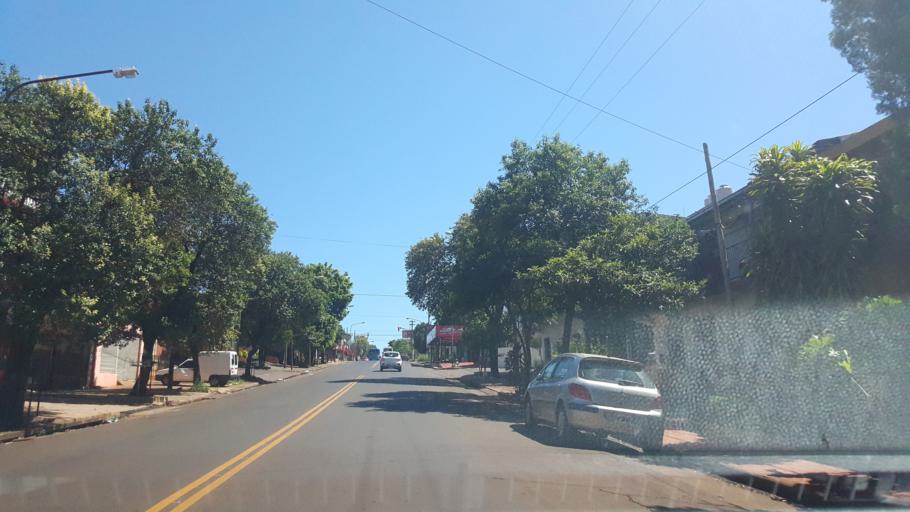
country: AR
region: Misiones
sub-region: Departamento de Capital
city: Posadas
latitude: -27.4018
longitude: -55.9100
